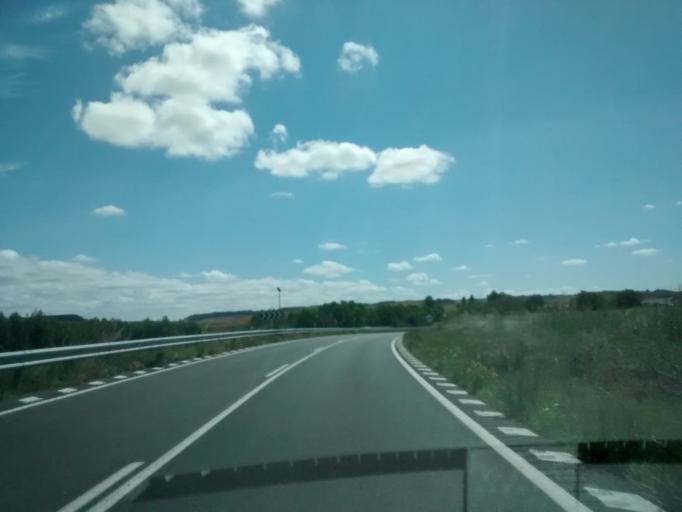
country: ES
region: La Rioja
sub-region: Provincia de La Rioja
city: Villamediana de Iregua
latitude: 42.4166
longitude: -2.3752
